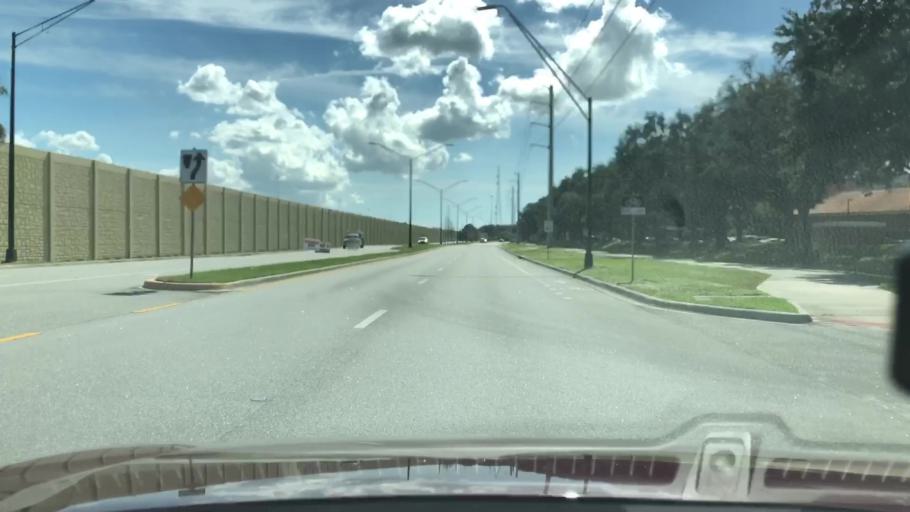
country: US
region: Florida
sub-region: Sarasota County
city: Fruitville
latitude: 27.3483
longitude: -82.4473
